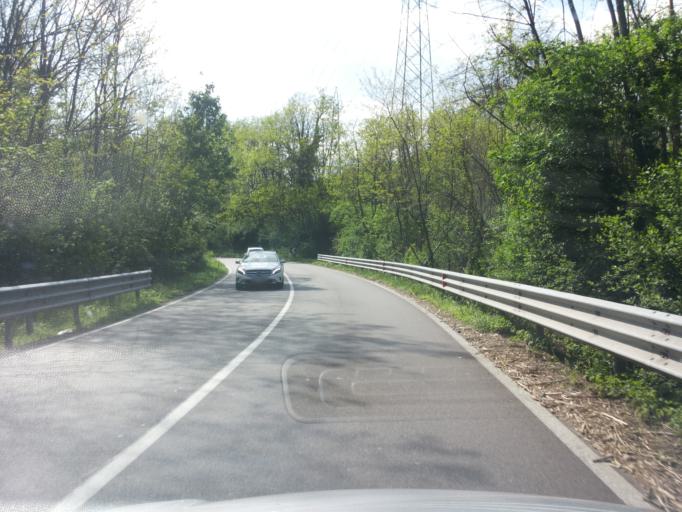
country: IT
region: Lombardy
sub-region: Provincia di Varese
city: Malnate
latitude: 45.8105
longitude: 8.8781
